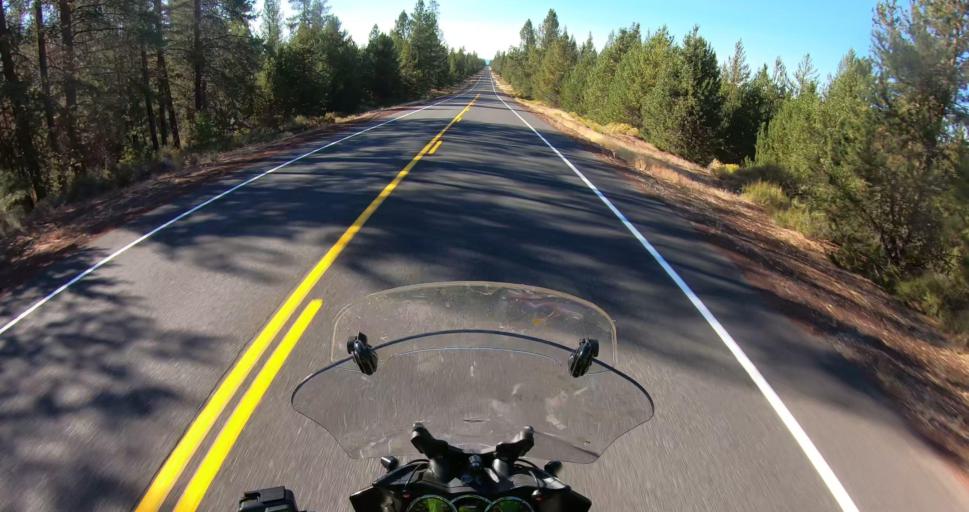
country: US
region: Oregon
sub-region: Deschutes County
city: La Pine
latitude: 43.4741
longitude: -121.4044
